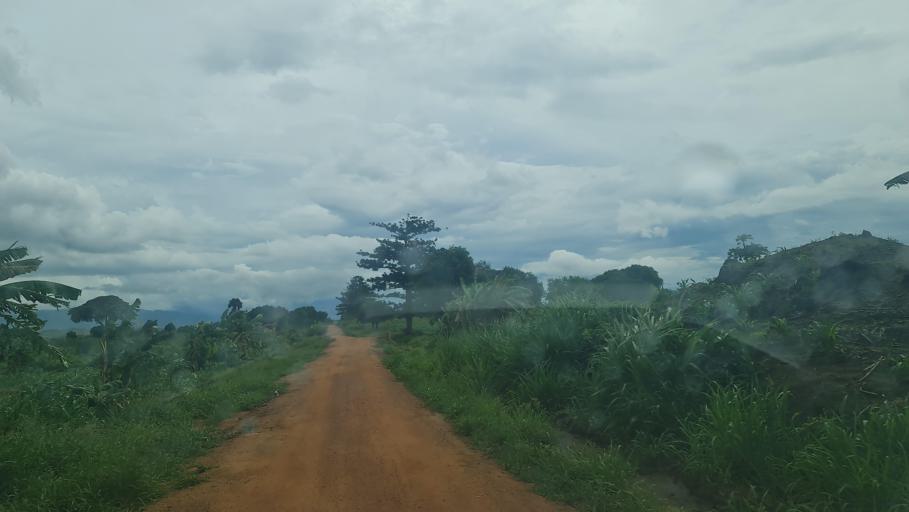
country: MW
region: Southern Region
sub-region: Nsanje District
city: Nsanje
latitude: -17.3955
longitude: 35.5763
